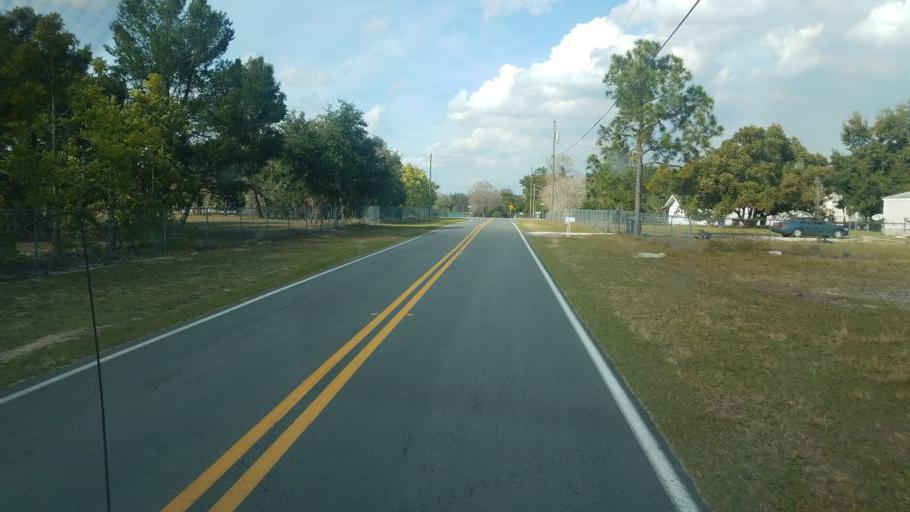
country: US
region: Florida
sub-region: Polk County
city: Davenport
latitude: 28.1494
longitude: -81.5657
